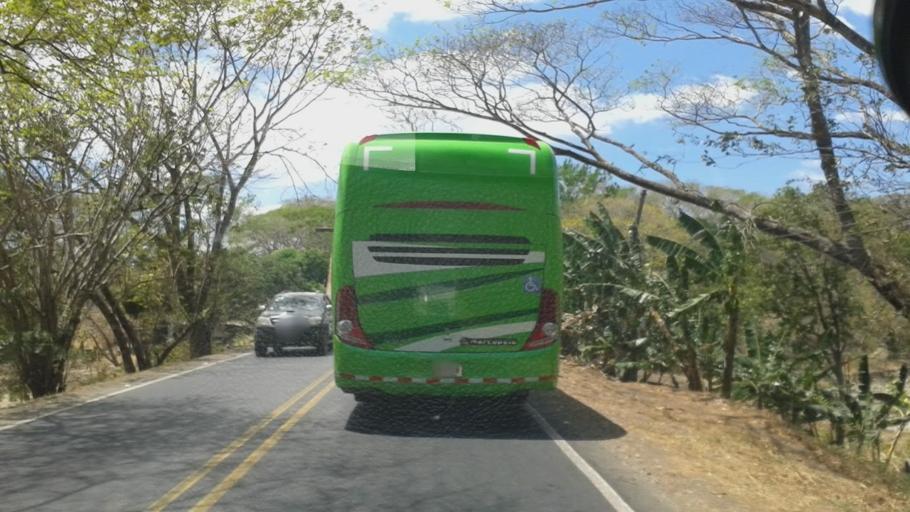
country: CR
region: Puntarenas
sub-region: Canton Central de Puntarenas
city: Puntarenas
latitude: 10.1026
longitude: -84.8735
